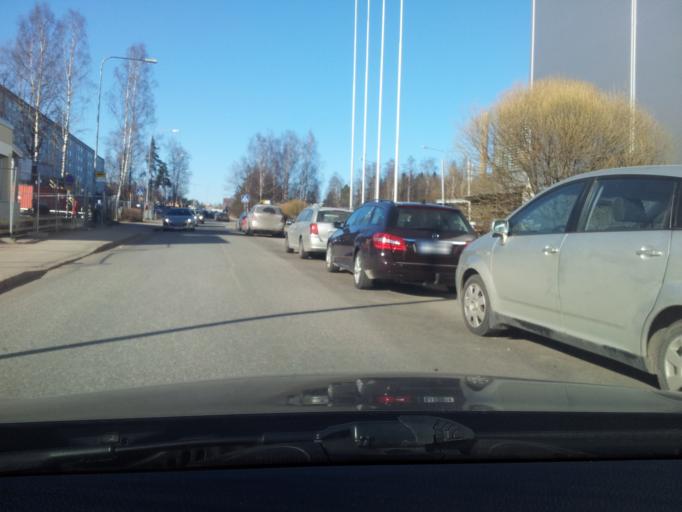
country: FI
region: Uusimaa
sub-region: Helsinki
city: Vantaa
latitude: 60.2209
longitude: 25.0790
